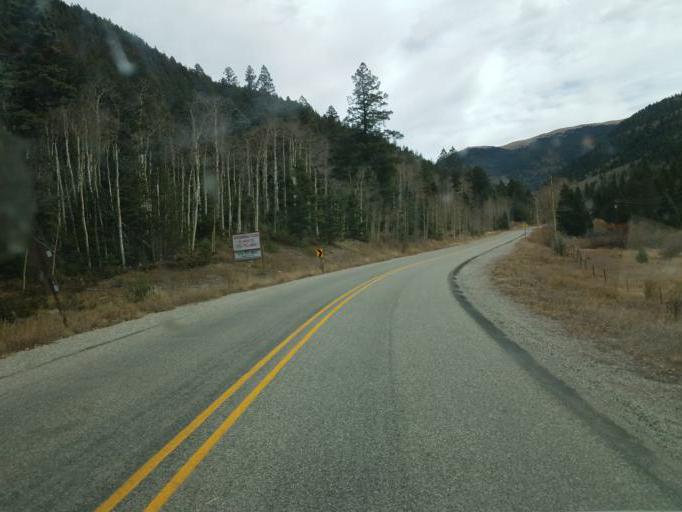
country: US
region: New Mexico
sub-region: Taos County
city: Arroyo Seco
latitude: 36.5958
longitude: -105.4771
